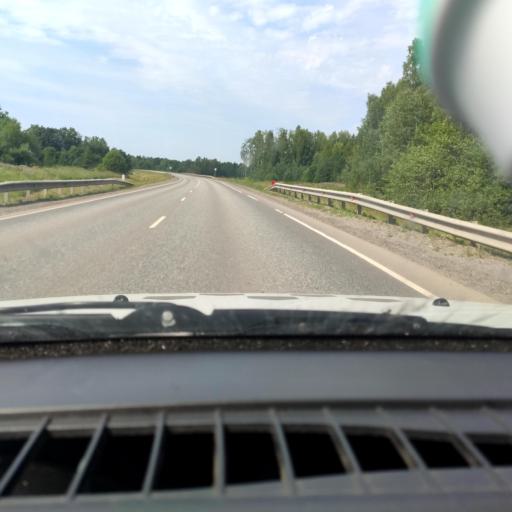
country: RU
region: Perm
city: Siva
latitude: 58.5026
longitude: 54.0433
